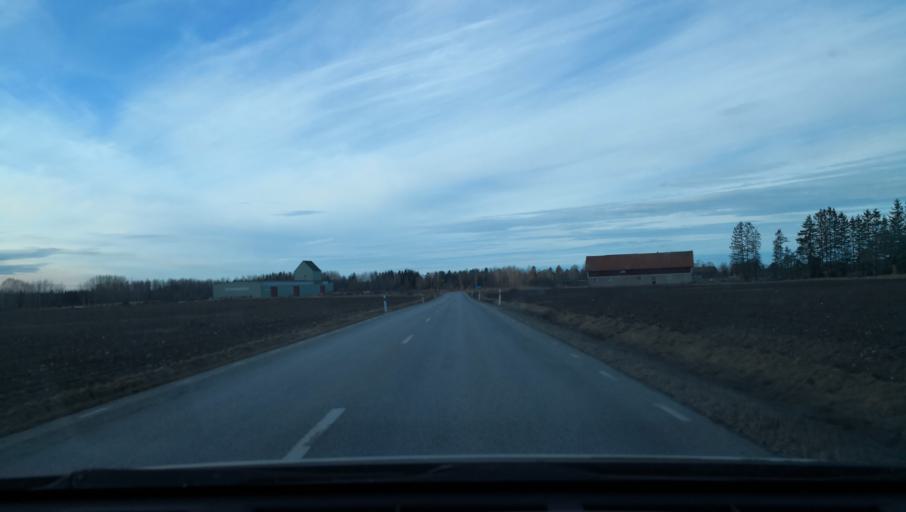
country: SE
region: Uppsala
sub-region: Osthammars Kommun
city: OEsthammar
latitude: 60.3189
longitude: 18.2589
